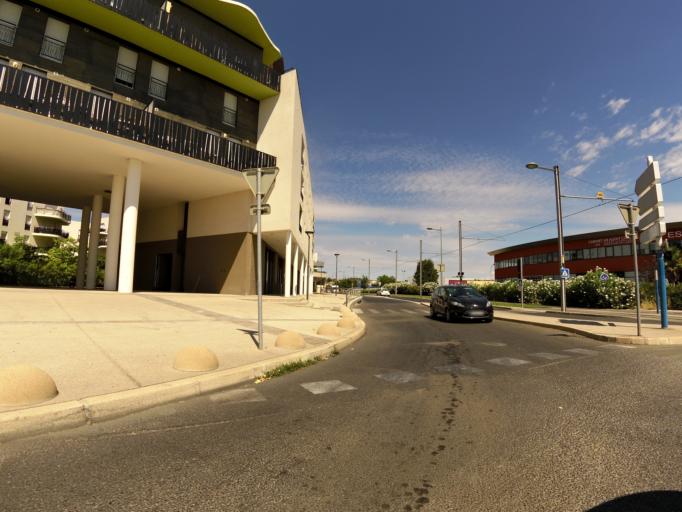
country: FR
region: Languedoc-Roussillon
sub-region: Departement de l'Herault
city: Le Cres
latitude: 43.6365
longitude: 3.9265
